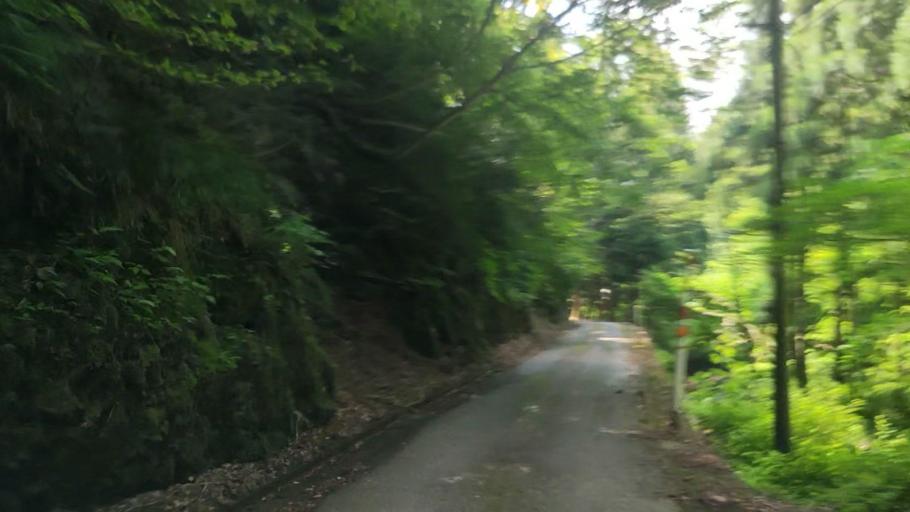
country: JP
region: Ishikawa
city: Komatsu
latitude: 36.2552
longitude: 136.5387
